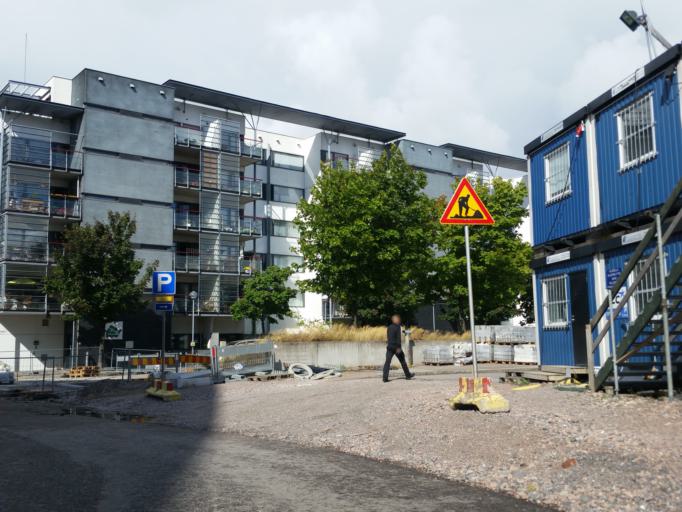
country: FI
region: Uusimaa
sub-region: Helsinki
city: Helsinki
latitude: 60.1606
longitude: 24.9199
